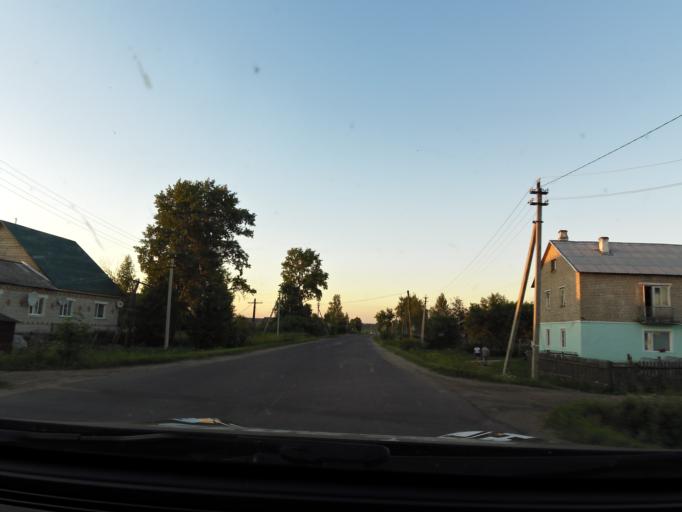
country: RU
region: Jaroslavl
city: Lyubim
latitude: 58.3614
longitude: 40.7038
